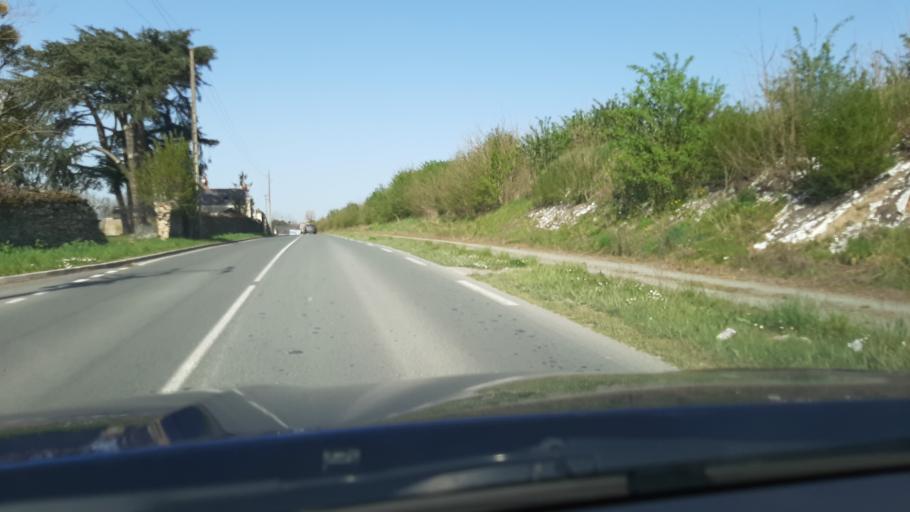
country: FR
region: Pays de la Loire
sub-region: Departement de Maine-et-Loire
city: Pellouailles-les-Vignes
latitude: 47.5130
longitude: -0.4531
